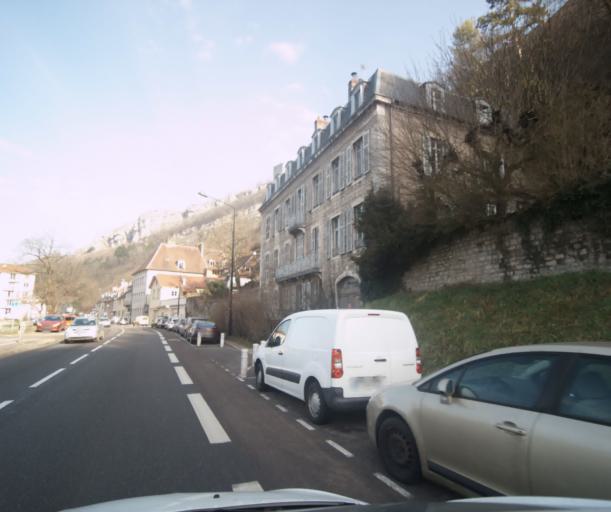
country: FR
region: Franche-Comte
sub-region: Departement du Doubs
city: Besancon
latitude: 47.2273
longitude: 6.0325
